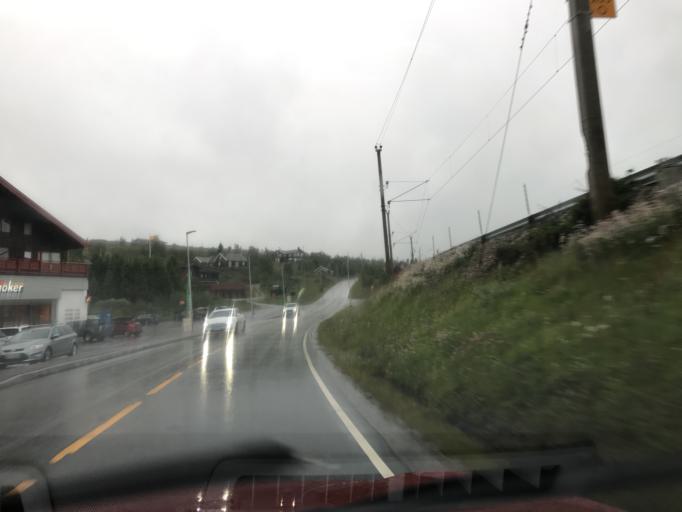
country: NO
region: Buskerud
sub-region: Hol
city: Geilo
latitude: 60.4989
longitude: 8.0408
